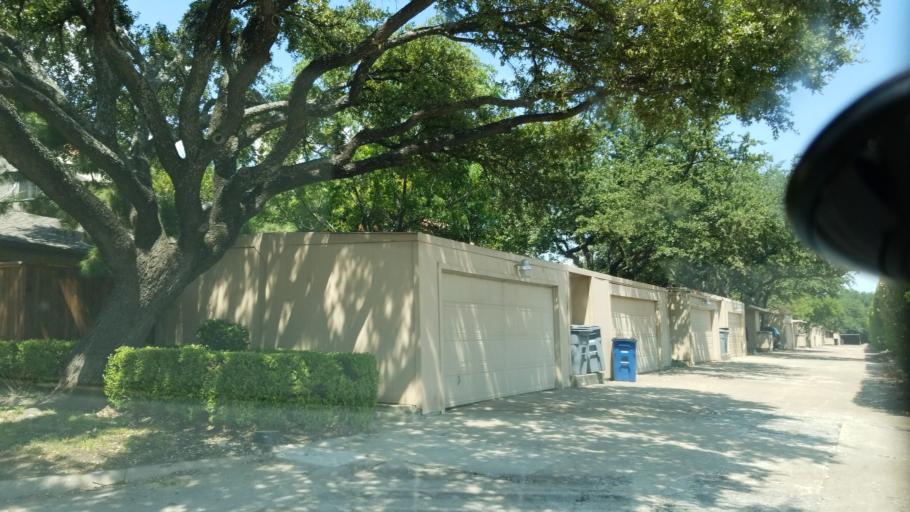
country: US
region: Texas
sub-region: Dallas County
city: Richardson
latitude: 32.9185
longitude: -96.7356
